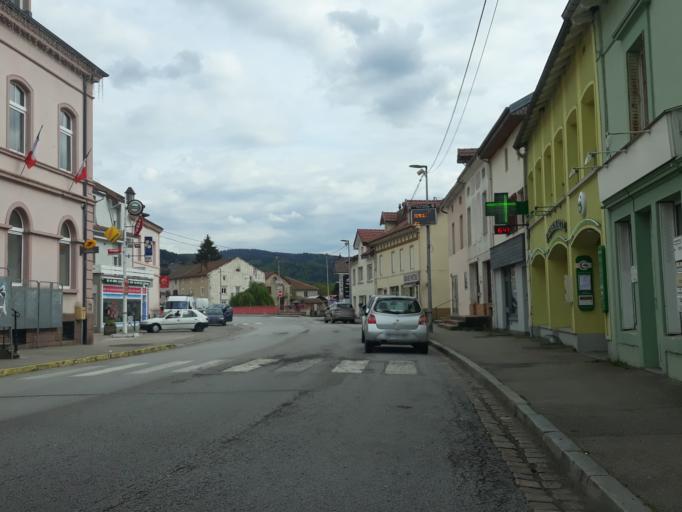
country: FR
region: Lorraine
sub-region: Departement des Vosges
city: Granges-sur-Vologne
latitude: 48.1448
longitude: 6.7891
